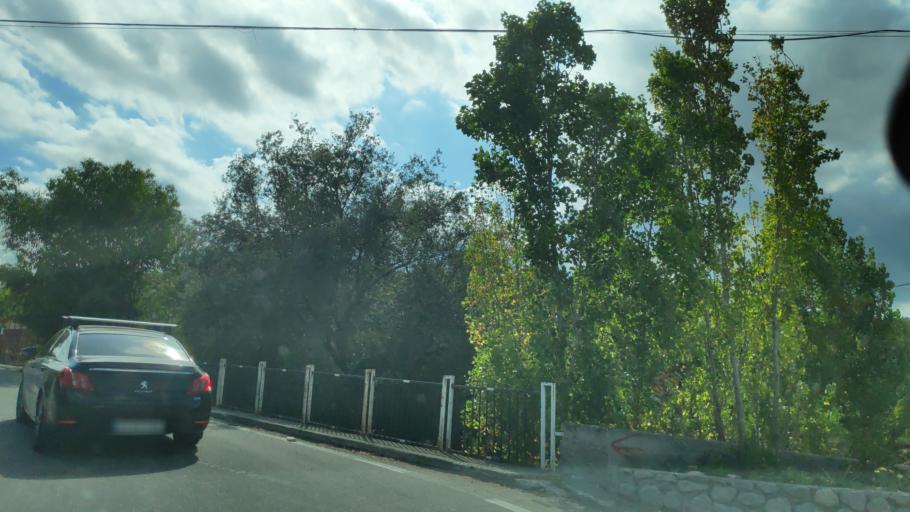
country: IT
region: Calabria
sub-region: Provincia di Catanzaro
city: Santa Caterina dello Ionio Marina
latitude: 38.5284
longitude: 16.5525
